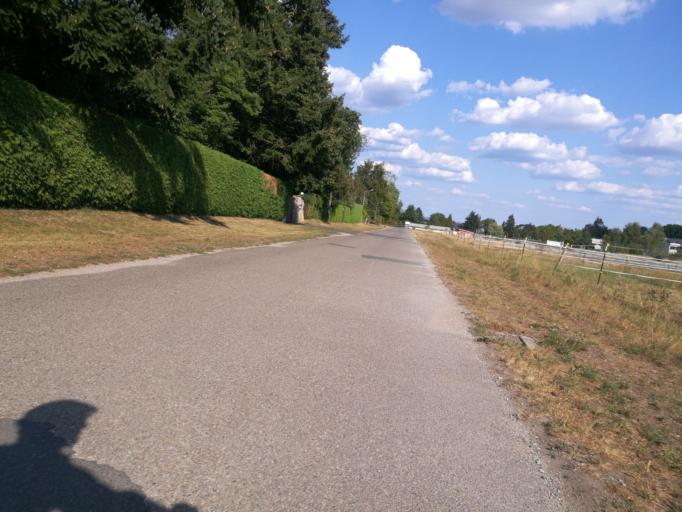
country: DE
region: Bavaria
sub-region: Regierungsbezirk Mittelfranken
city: Zirndorf
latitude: 49.4721
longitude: 10.9339
